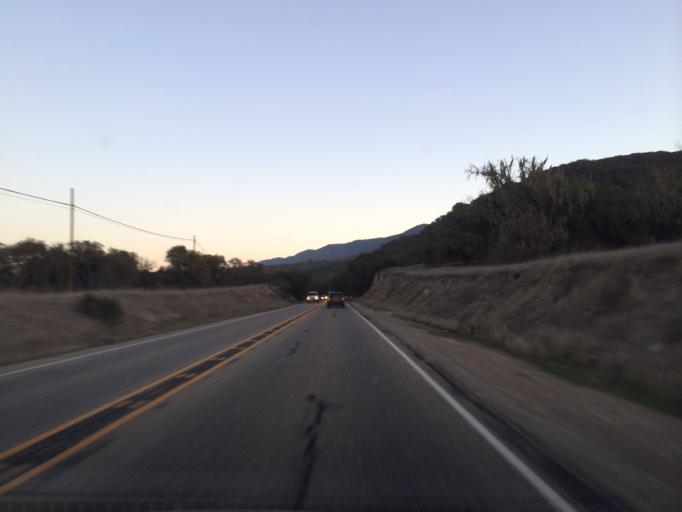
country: US
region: California
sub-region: Santa Barbara County
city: Santa Ynez
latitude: 34.5820
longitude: -119.9906
